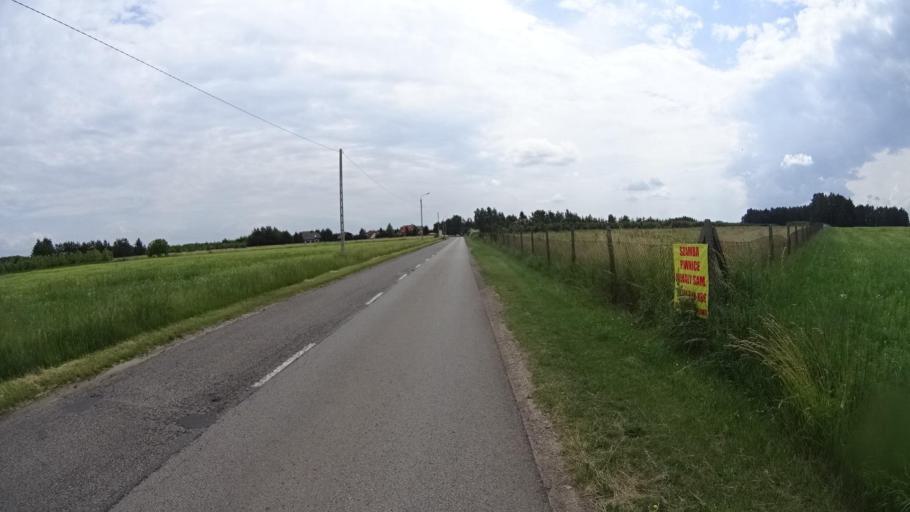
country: PL
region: Masovian Voivodeship
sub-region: Powiat piaseczynski
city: Tarczyn
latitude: 52.0044
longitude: 20.8120
